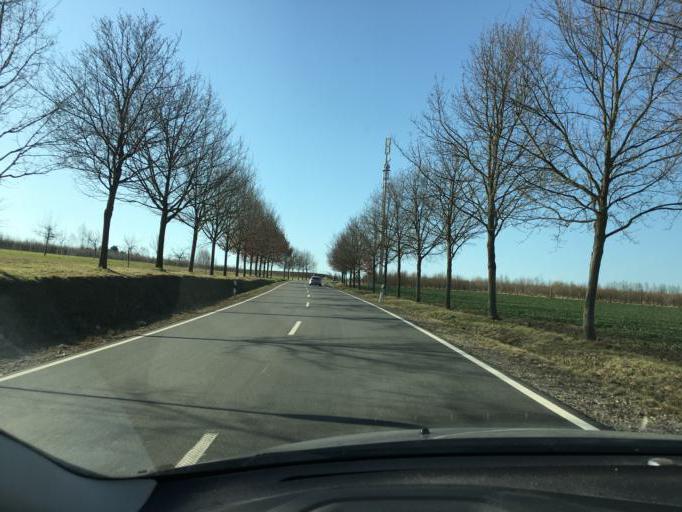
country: DE
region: Saxony
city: Hohenstein-Ernstthal
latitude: 50.8128
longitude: 12.7042
